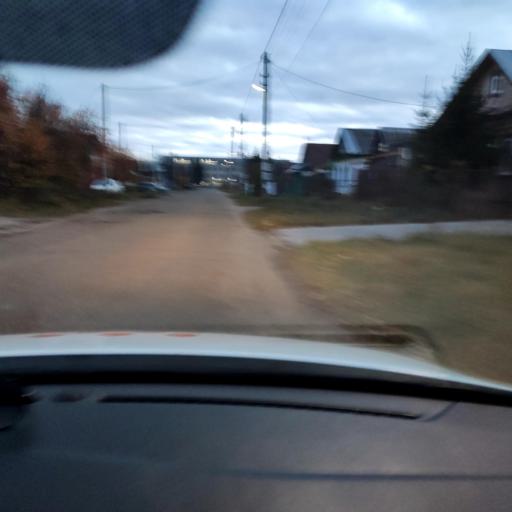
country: RU
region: Tatarstan
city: Staroye Arakchino
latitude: 55.8684
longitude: 49.0272
